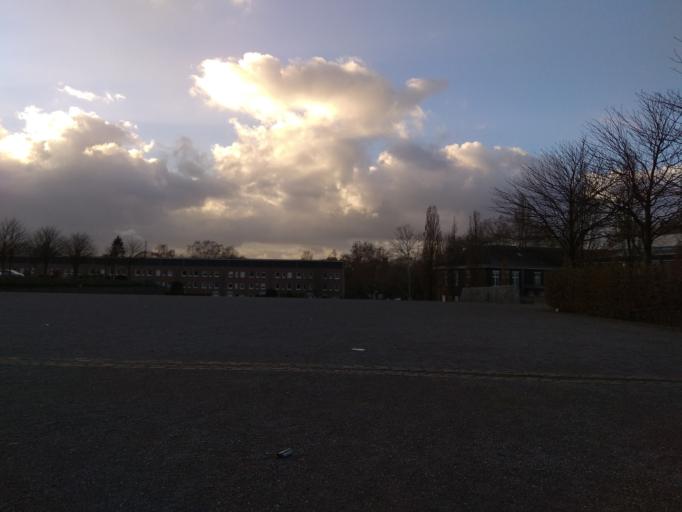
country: DE
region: North Rhine-Westphalia
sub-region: Regierungsbezirk Munster
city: Gladbeck
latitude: 51.5279
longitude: 7.0300
